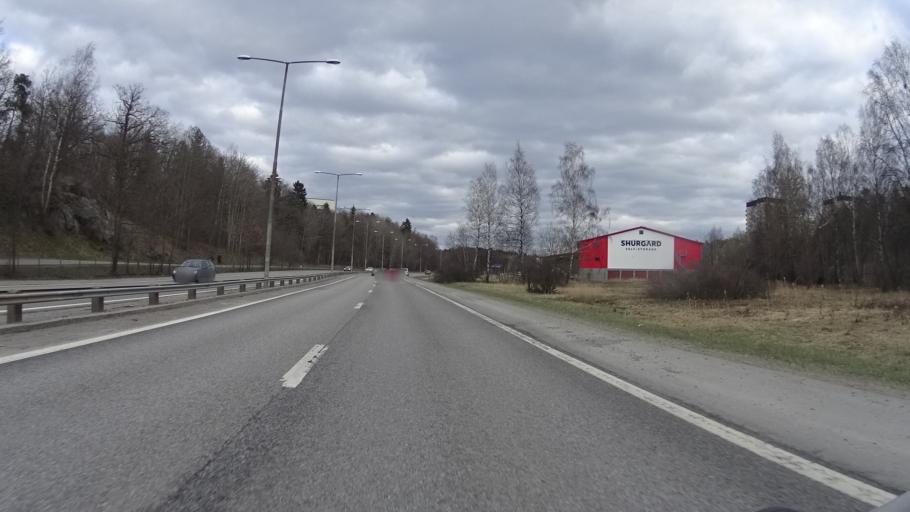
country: SE
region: Stockholm
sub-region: Stockholms Kommun
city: Arsta
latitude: 59.2628
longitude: 18.0291
